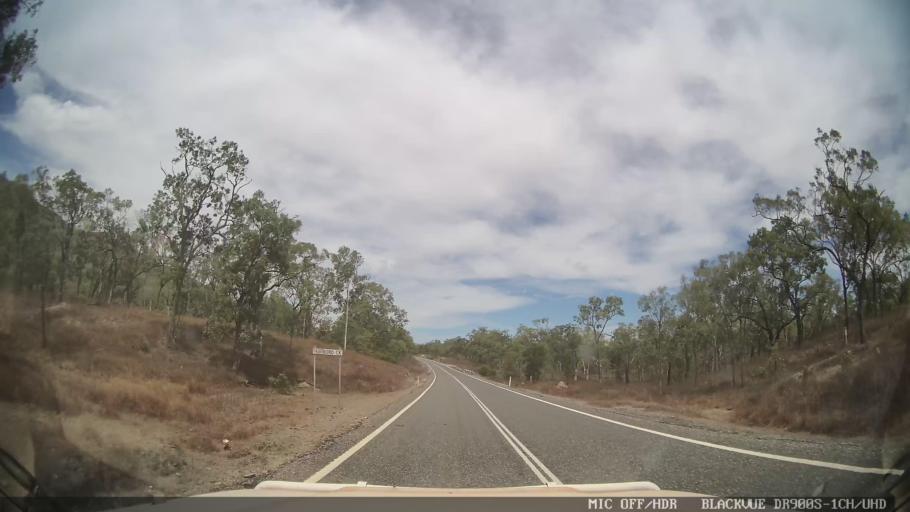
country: AU
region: Queensland
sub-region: Cairns
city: Port Douglas
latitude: -16.3539
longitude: 144.7266
